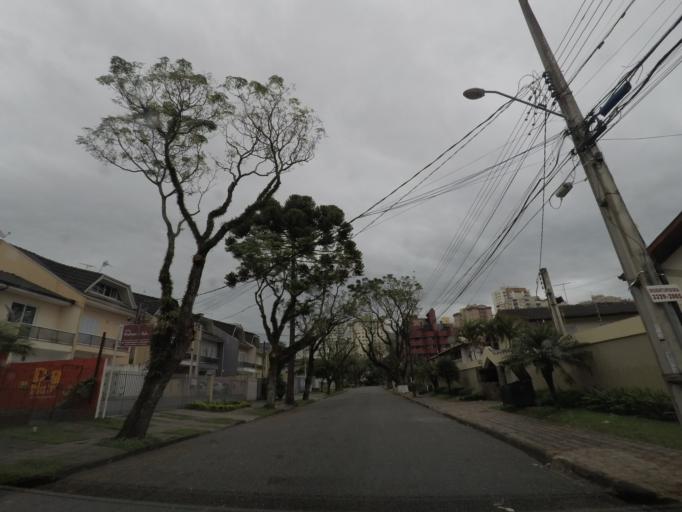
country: BR
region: Parana
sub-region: Curitiba
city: Curitiba
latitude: -25.4575
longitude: -49.2840
